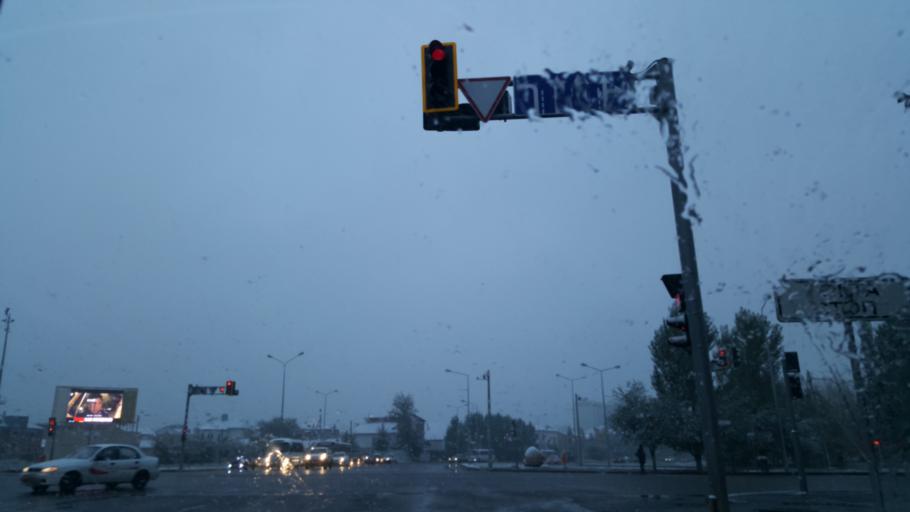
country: KZ
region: Astana Qalasy
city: Astana
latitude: 51.1481
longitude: 71.5041
